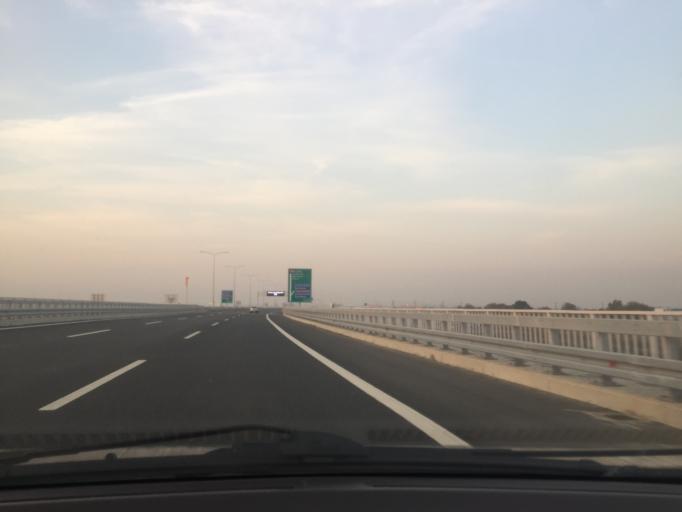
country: TR
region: Bursa
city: Karacabey
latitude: 40.2002
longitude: 28.3729
